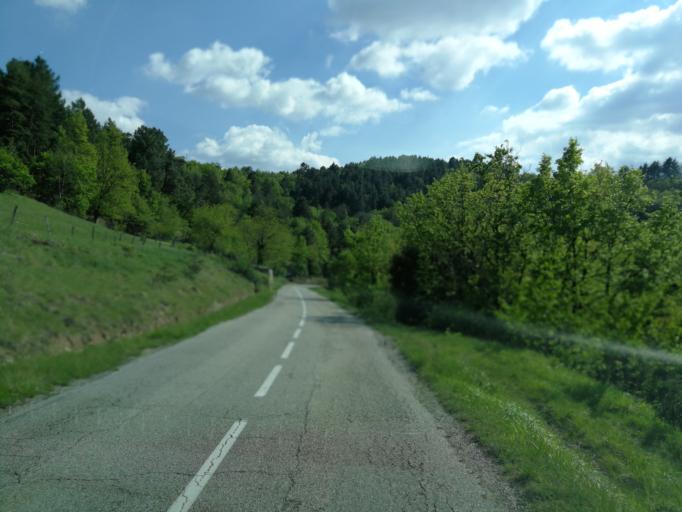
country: FR
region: Rhone-Alpes
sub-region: Departement de l'Ardeche
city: Saint-Sauveur-de-Montagut
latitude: 44.7891
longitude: 4.6169
